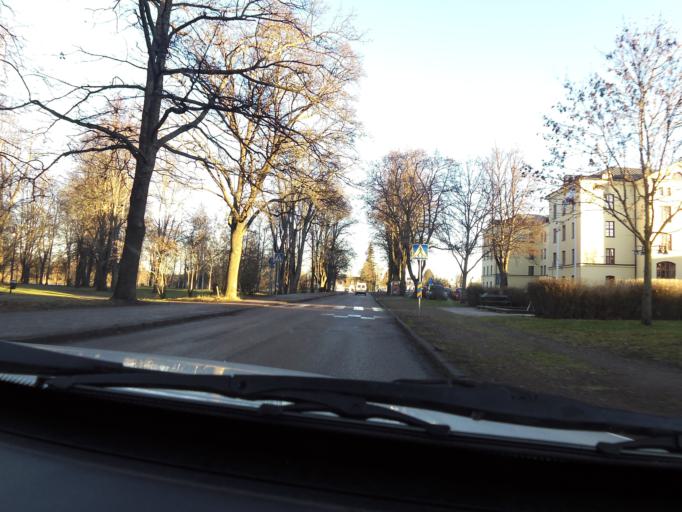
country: SE
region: Gaevleborg
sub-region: Gavle Kommun
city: Gavle
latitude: 60.6689
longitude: 17.1176
